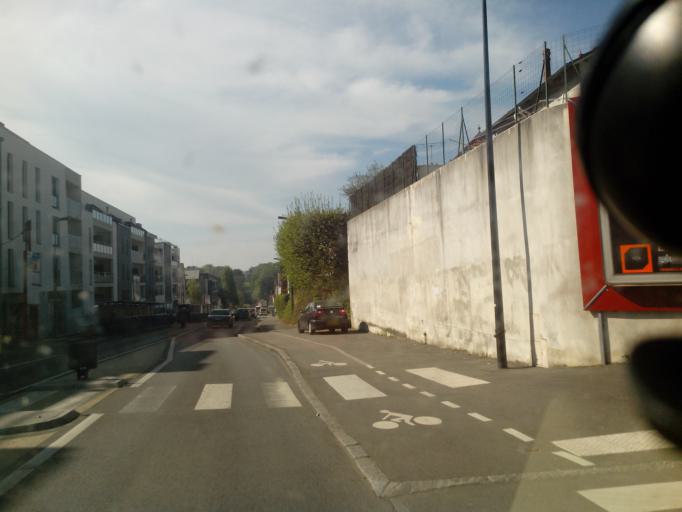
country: FR
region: Pays de la Loire
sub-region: Departement de la Loire-Atlantique
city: Nantes
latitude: 47.2524
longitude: -1.5764
